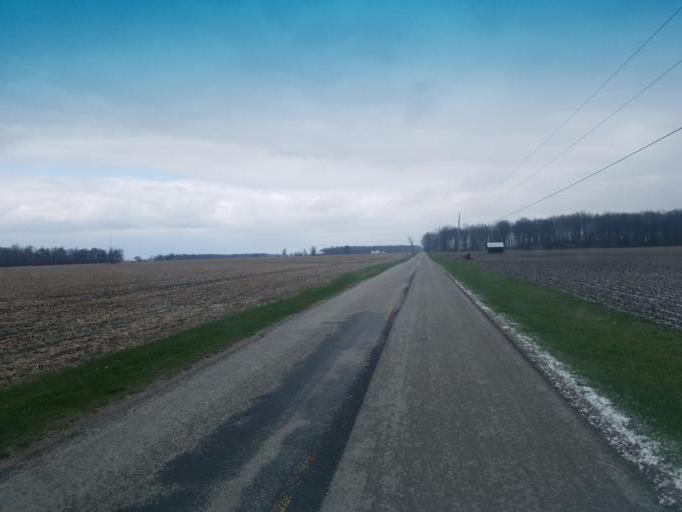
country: US
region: Ohio
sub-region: Marion County
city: Prospect
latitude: 40.4187
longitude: -83.1153
